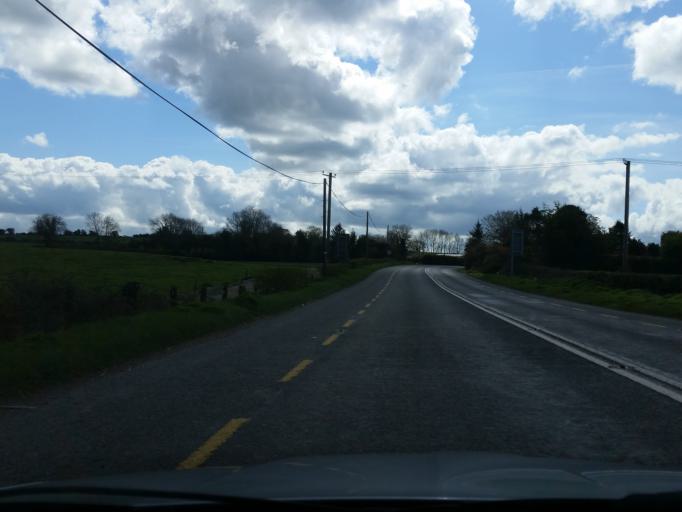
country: IE
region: Leinster
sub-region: An Mhi
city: Slane
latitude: 53.6955
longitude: -6.5389
